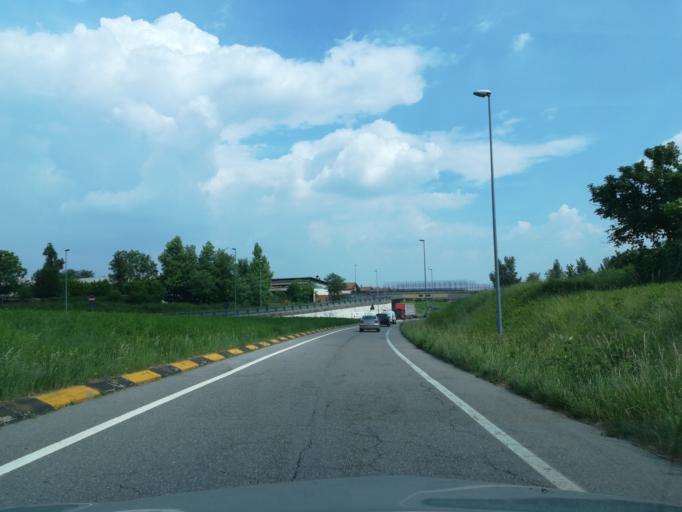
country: IT
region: Lombardy
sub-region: Provincia di Bergamo
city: Brusaporto
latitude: 45.6689
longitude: 9.7540
